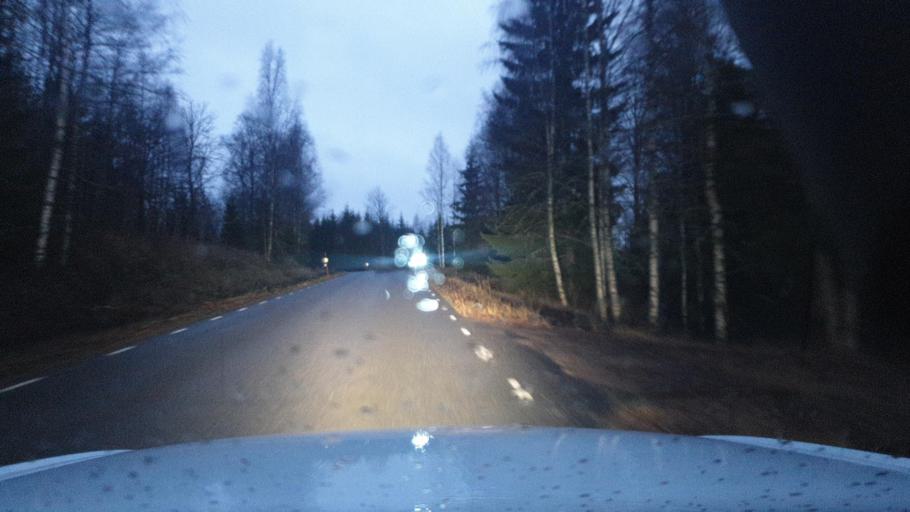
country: SE
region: Vaermland
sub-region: Torsby Kommun
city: Torsby
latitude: 60.0110
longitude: 12.6756
